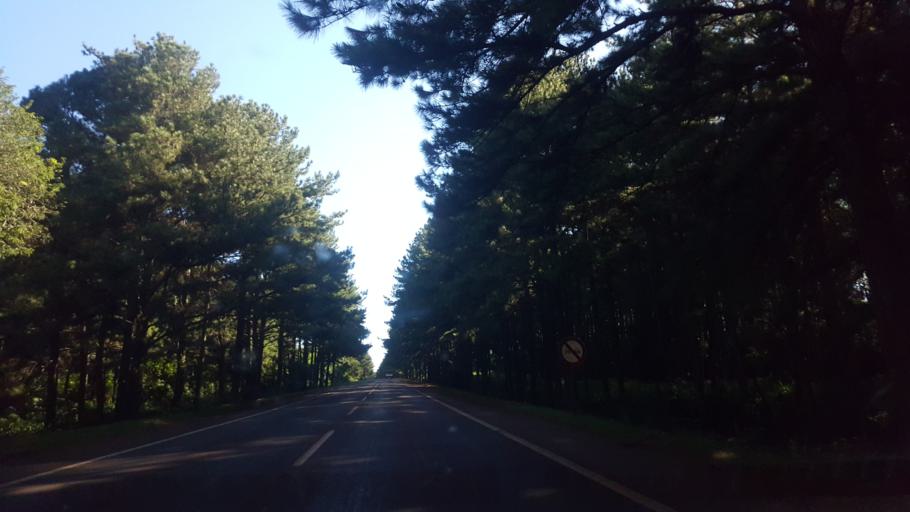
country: AR
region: Misiones
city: Puerto Libertad
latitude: -25.9036
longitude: -54.5627
